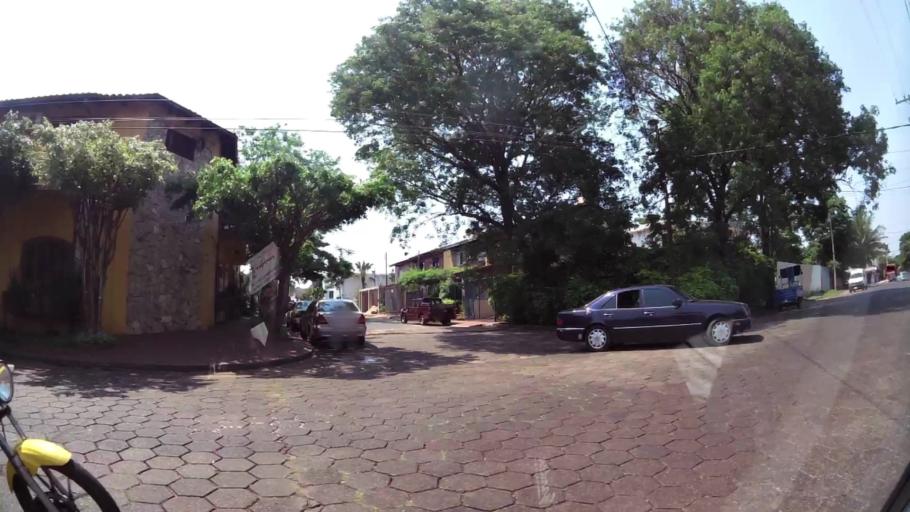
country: PY
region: Alto Parana
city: Presidente Franco
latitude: -25.5243
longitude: -54.6203
